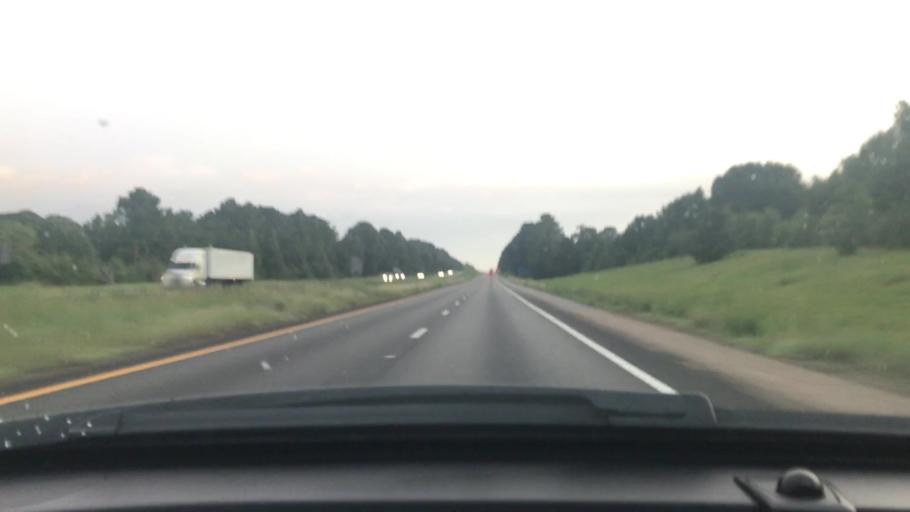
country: US
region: Louisiana
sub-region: Tangipahoa Parish
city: Kentwood
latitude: 31.0030
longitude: -90.5053
